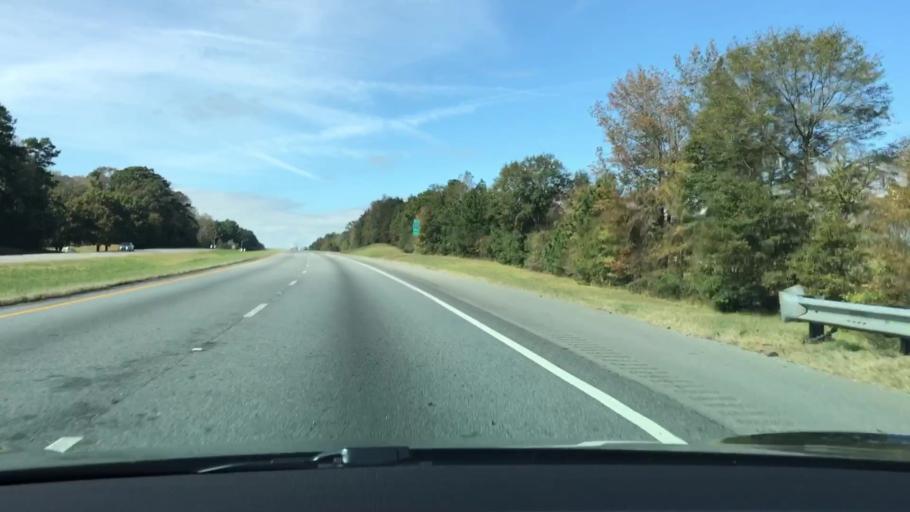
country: US
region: Georgia
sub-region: Walton County
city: Social Circle
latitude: 33.6029
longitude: -83.6597
